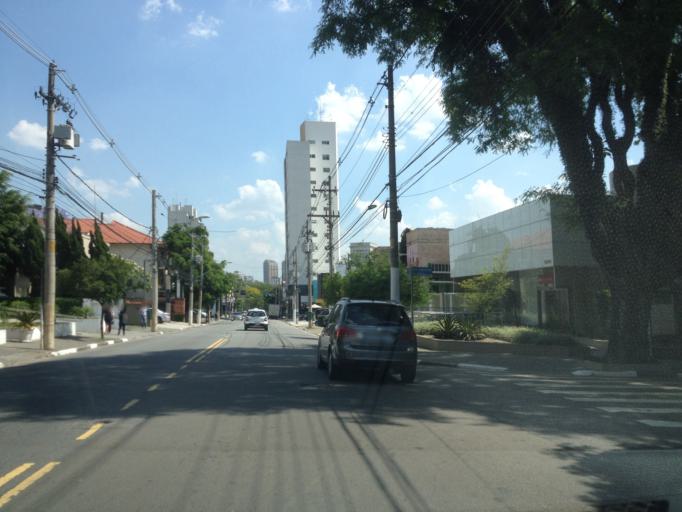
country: BR
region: Sao Paulo
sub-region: Sao Paulo
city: Sao Paulo
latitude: -23.5700
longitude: -46.6801
